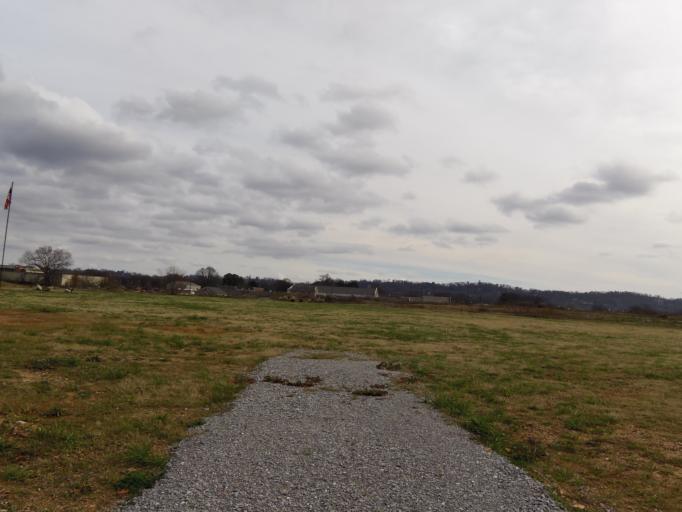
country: US
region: Tennessee
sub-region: Hamilton County
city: Chattanooga
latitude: 35.0262
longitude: -85.2937
